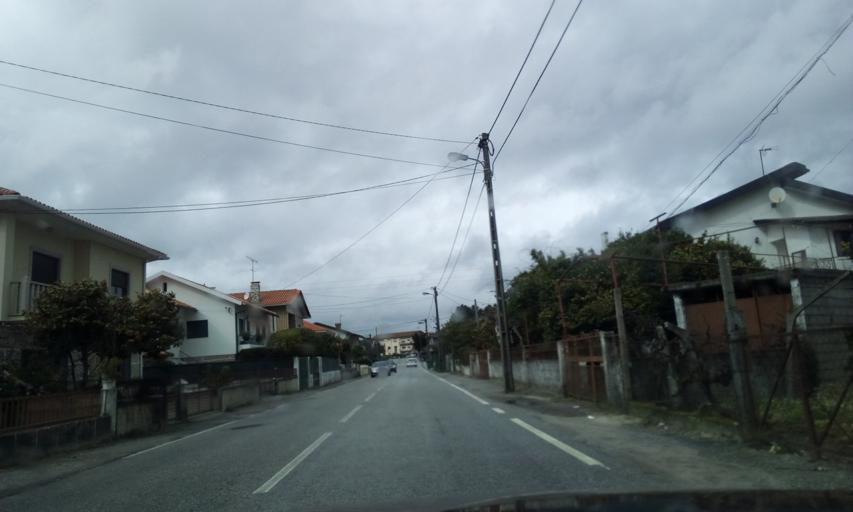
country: PT
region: Viseu
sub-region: Viseu
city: Rio de Loba
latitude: 40.6420
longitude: -7.8661
